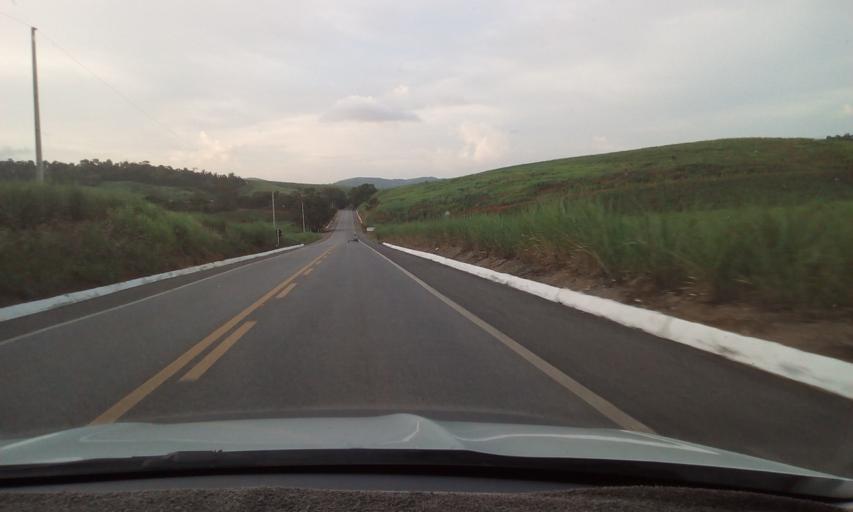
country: BR
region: Pernambuco
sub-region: Vicencia
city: Vicencia
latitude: -7.6486
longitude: -35.2524
